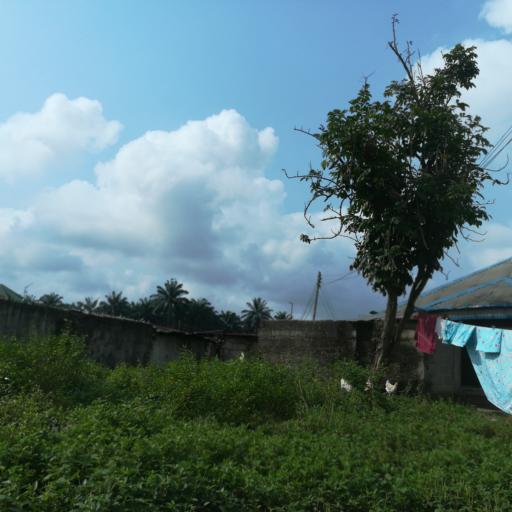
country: NG
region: Rivers
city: Okrika
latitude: 4.7854
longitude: 7.1181
